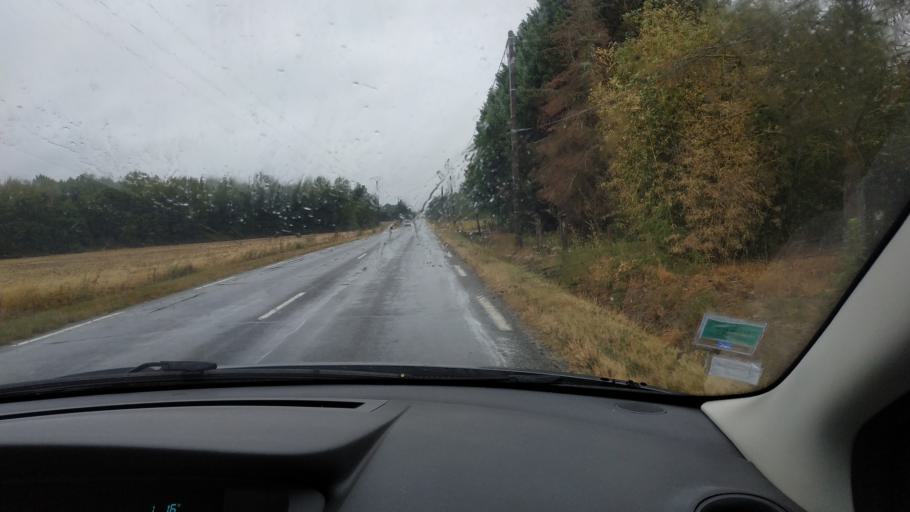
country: FR
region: Centre
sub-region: Departement du Loiret
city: Bellegarde
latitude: 47.9308
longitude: 2.3916
